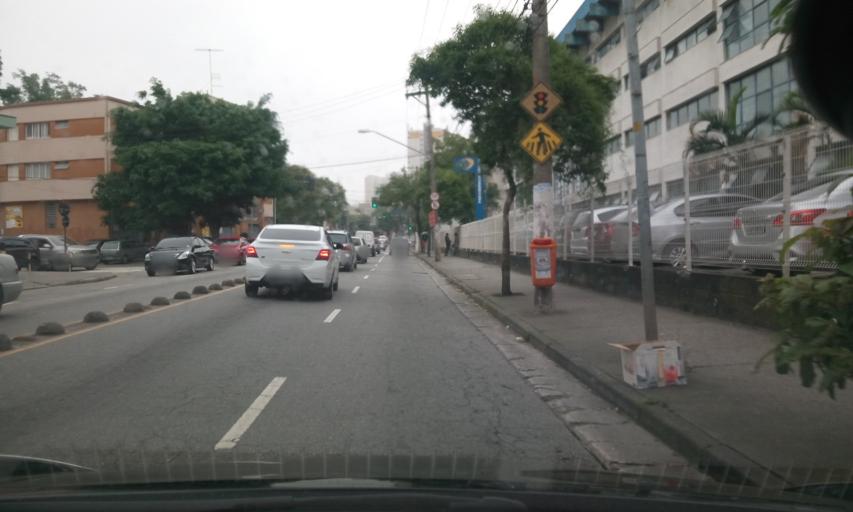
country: BR
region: Sao Paulo
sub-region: Sao Bernardo Do Campo
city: Sao Bernardo do Campo
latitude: -23.7041
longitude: -46.5553
